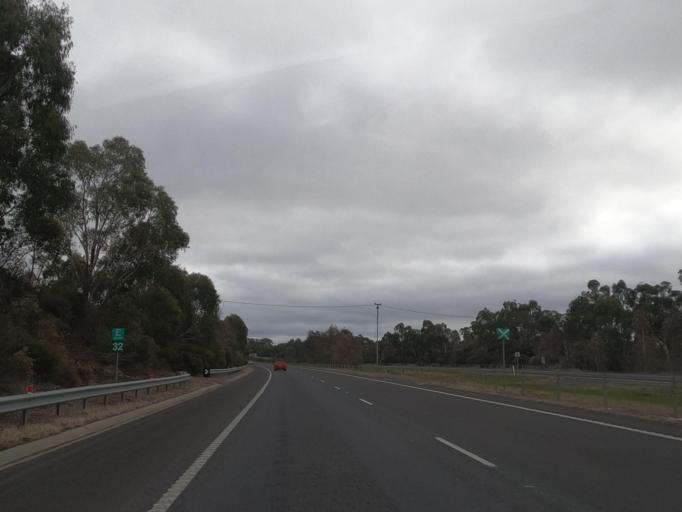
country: AU
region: Victoria
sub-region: Mount Alexander
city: Castlemaine
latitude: -37.0970
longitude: 144.3600
